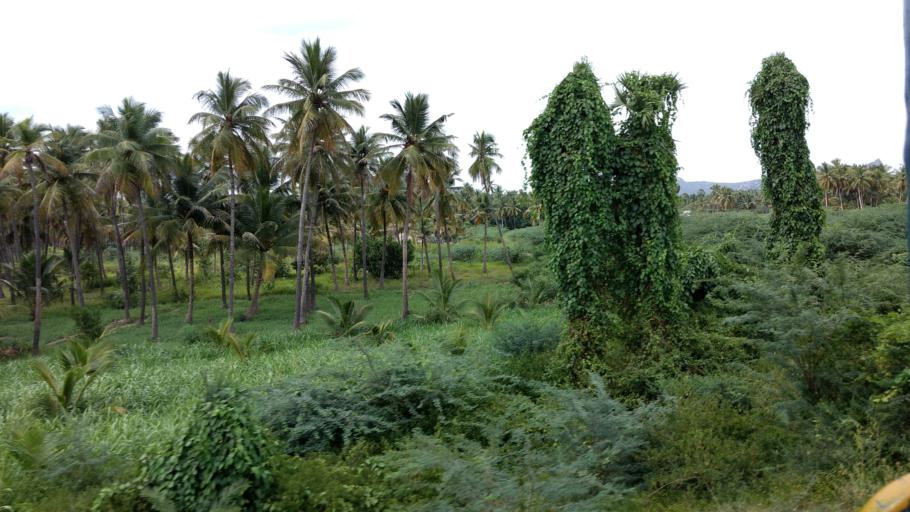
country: IN
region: Tamil Nadu
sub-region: Vellore
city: Gudiyatham
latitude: 12.9244
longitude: 78.8850
